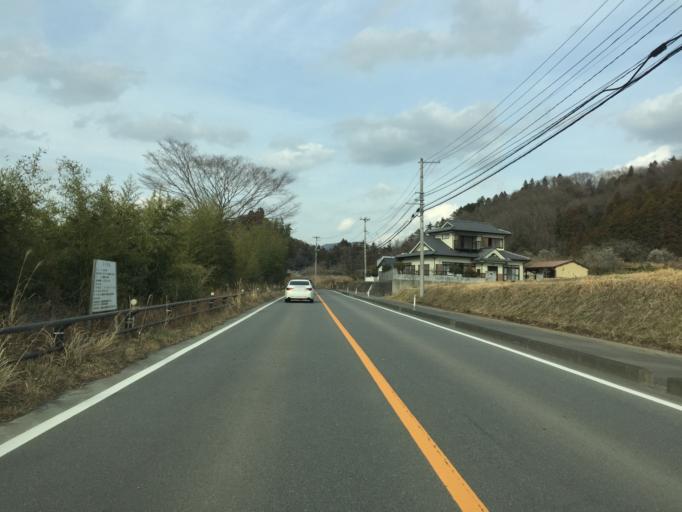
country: JP
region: Fukushima
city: Iwaki
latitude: 36.9861
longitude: 140.7372
